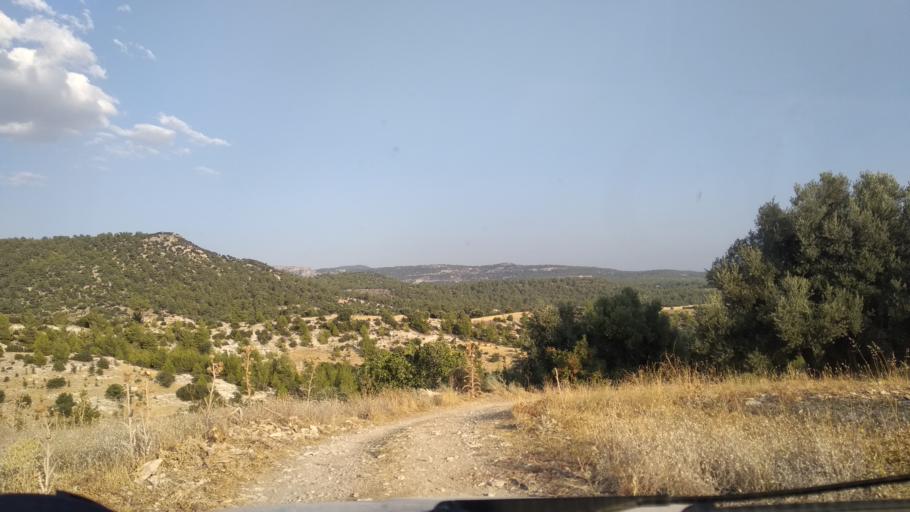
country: TR
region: Mersin
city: Sarikavak
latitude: 36.5607
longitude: 33.6277
